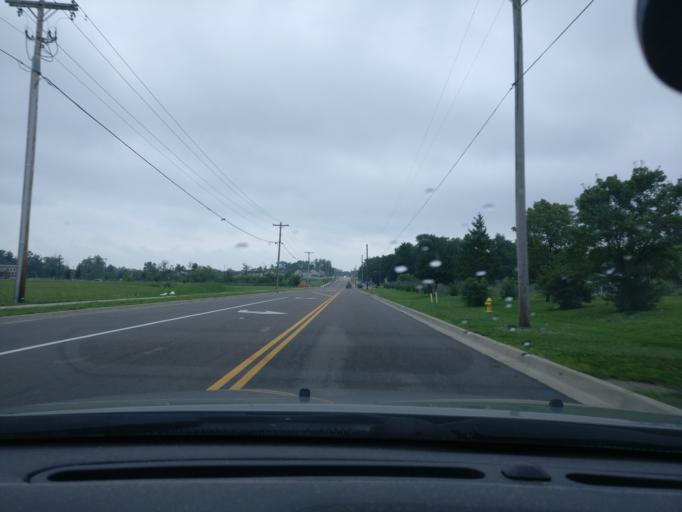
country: US
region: Ohio
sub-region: Warren County
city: Springboro
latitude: 39.5891
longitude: -84.2483
